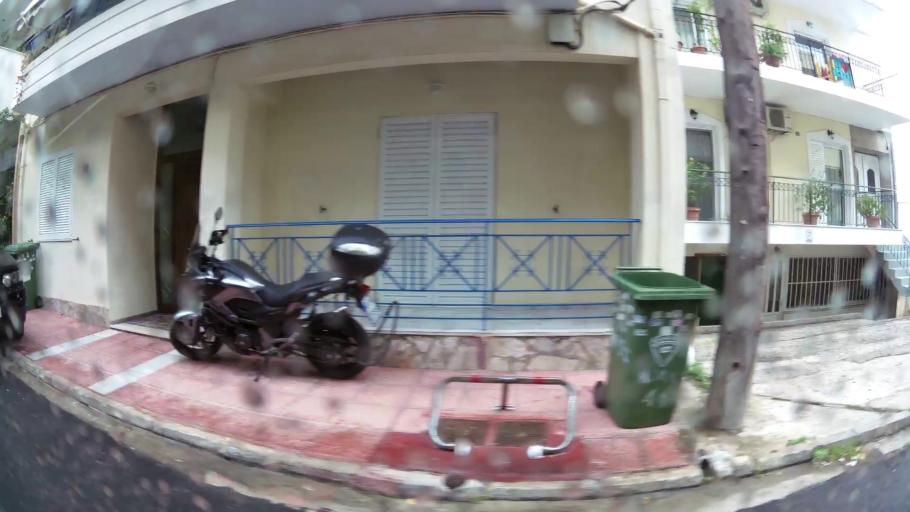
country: GR
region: Attica
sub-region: Nomos Piraios
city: Korydallos
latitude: 38.0021
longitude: 23.6445
